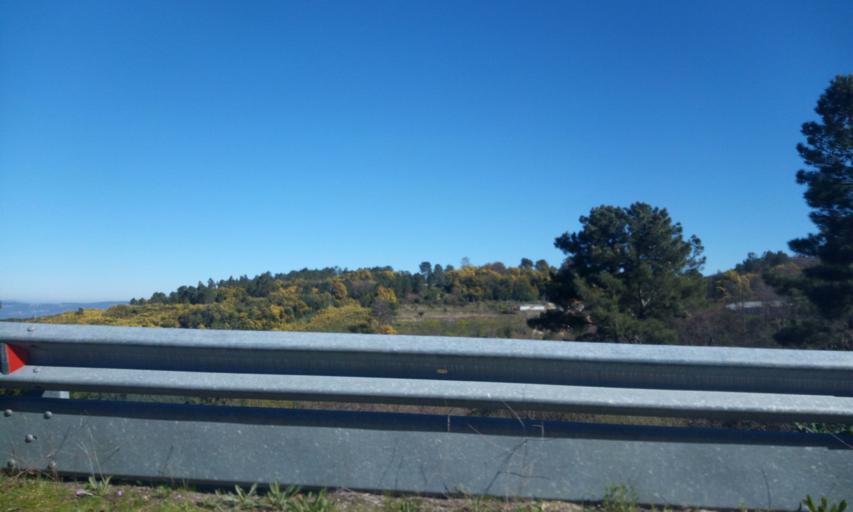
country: PT
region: Guarda
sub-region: Manteigas
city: Manteigas
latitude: 40.5052
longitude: -7.5752
